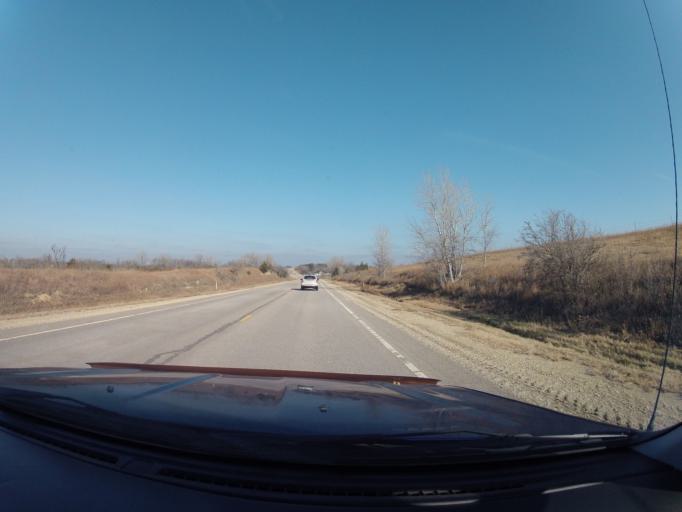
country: US
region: Kansas
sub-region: Marshall County
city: Blue Rapids
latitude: 39.5767
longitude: -96.7503
